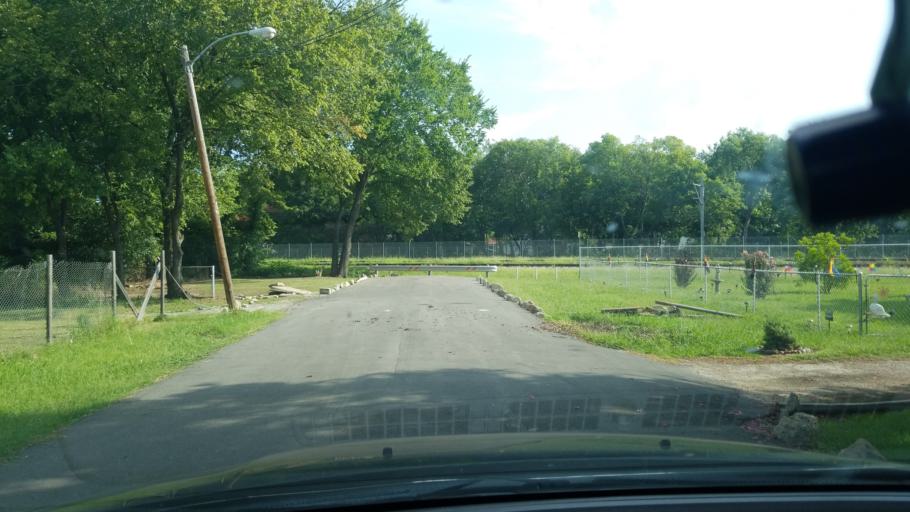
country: US
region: Texas
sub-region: Dallas County
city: Balch Springs
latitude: 32.7215
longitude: -96.6911
